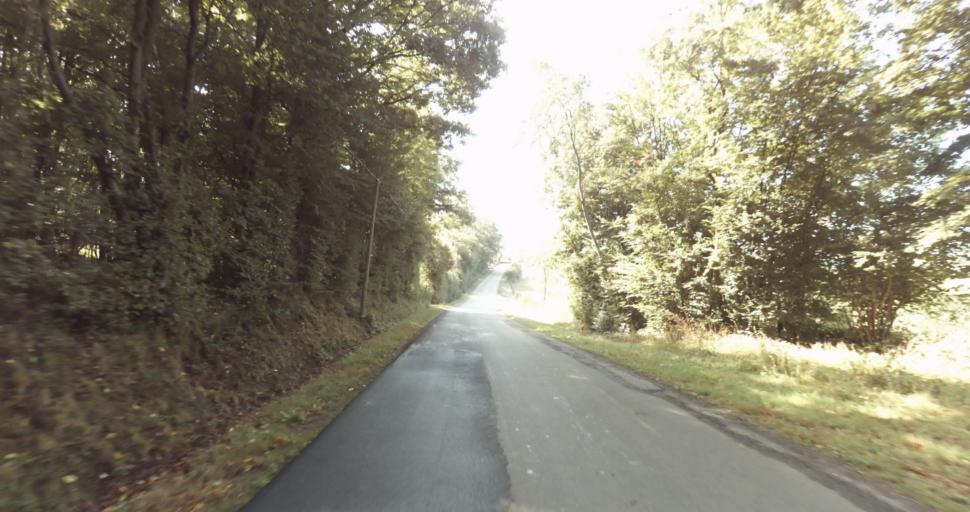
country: FR
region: Lower Normandy
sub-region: Departement du Calvados
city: Orbec
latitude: 48.9219
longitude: 0.3435
